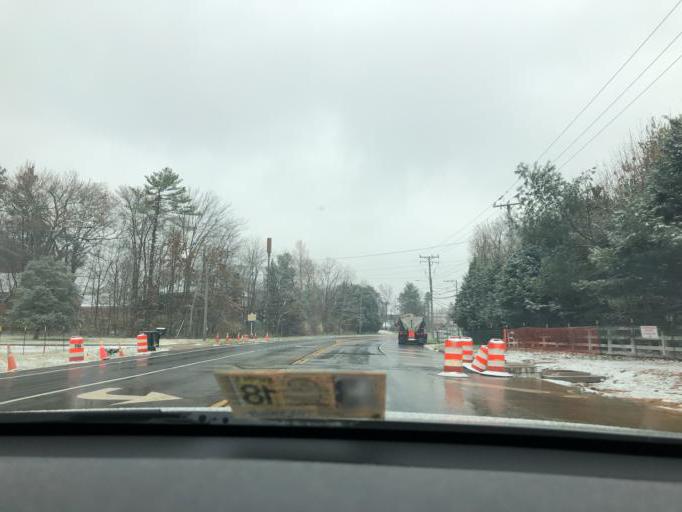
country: US
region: Virginia
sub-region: Fairfax County
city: Oakton
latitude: 38.8868
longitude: -77.3019
